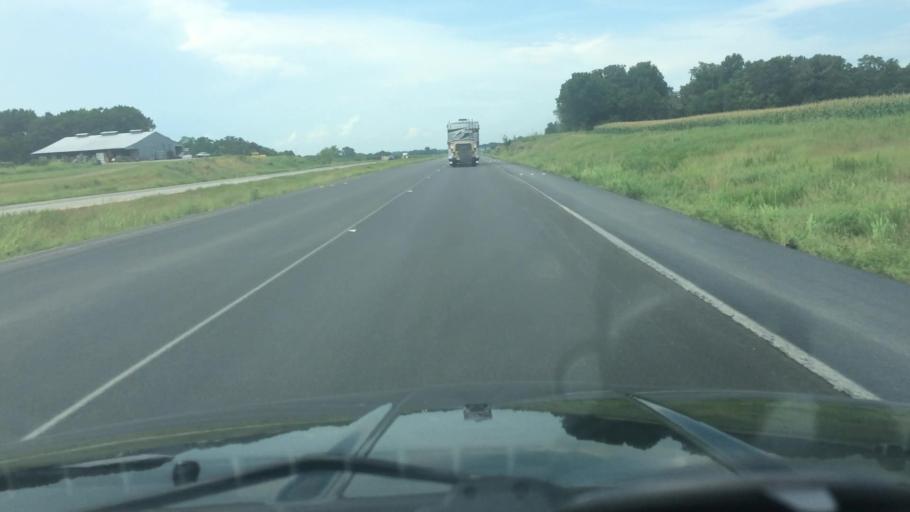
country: US
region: Missouri
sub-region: Saint Clair County
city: Osceola
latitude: 37.9789
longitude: -93.6487
